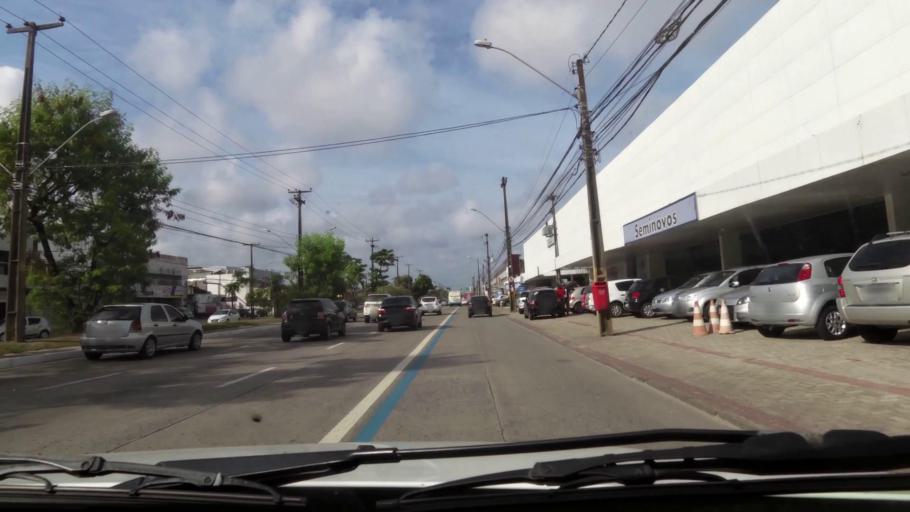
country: BR
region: Pernambuco
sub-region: Recife
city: Recife
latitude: -8.0911
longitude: -34.9084
